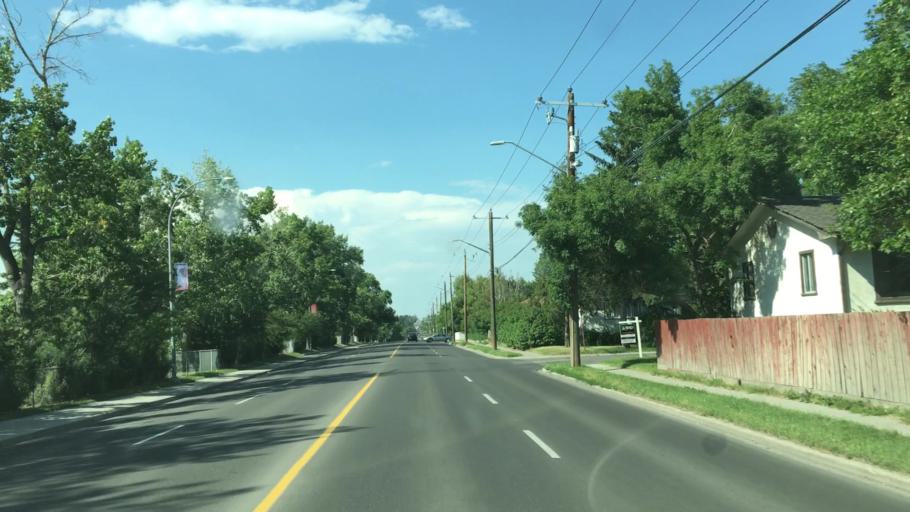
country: CA
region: Alberta
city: Calgary
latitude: 51.0820
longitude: -114.0715
